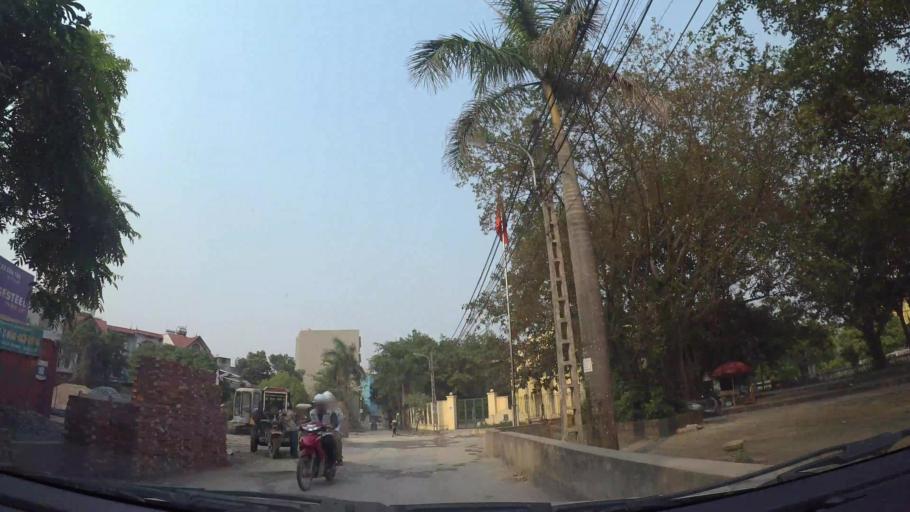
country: VN
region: Ha Noi
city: Ha Dong
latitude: 20.9999
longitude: 105.7451
